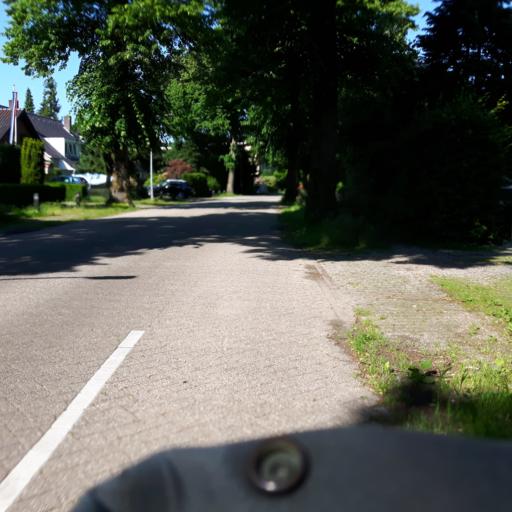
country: NL
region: Utrecht
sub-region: Gemeente Zeist
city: Zeist
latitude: 52.1372
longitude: 5.2421
